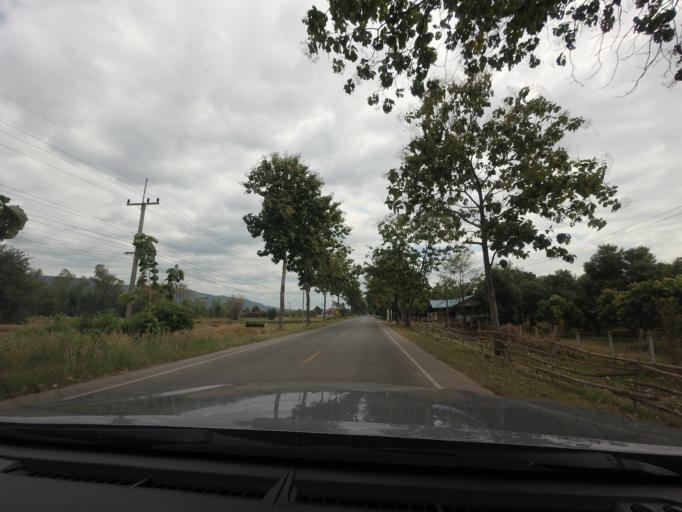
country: TH
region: Phitsanulok
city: Wang Thong
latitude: 16.7115
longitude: 100.4785
